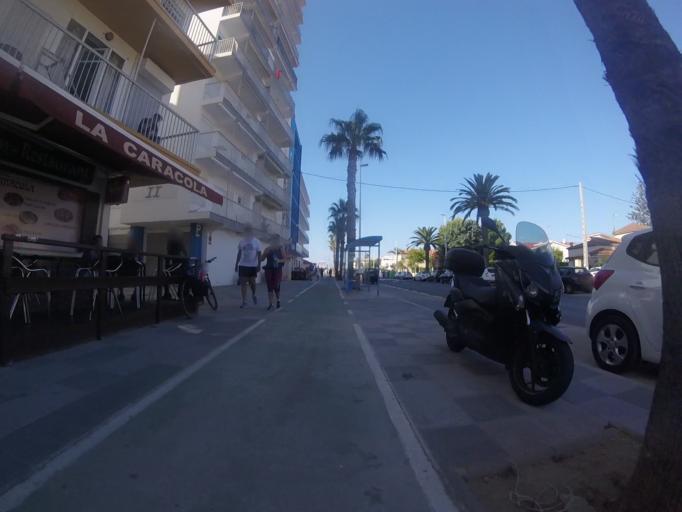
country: ES
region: Valencia
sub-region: Provincia de Castello
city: Benicarlo
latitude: 40.4014
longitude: 0.4179
